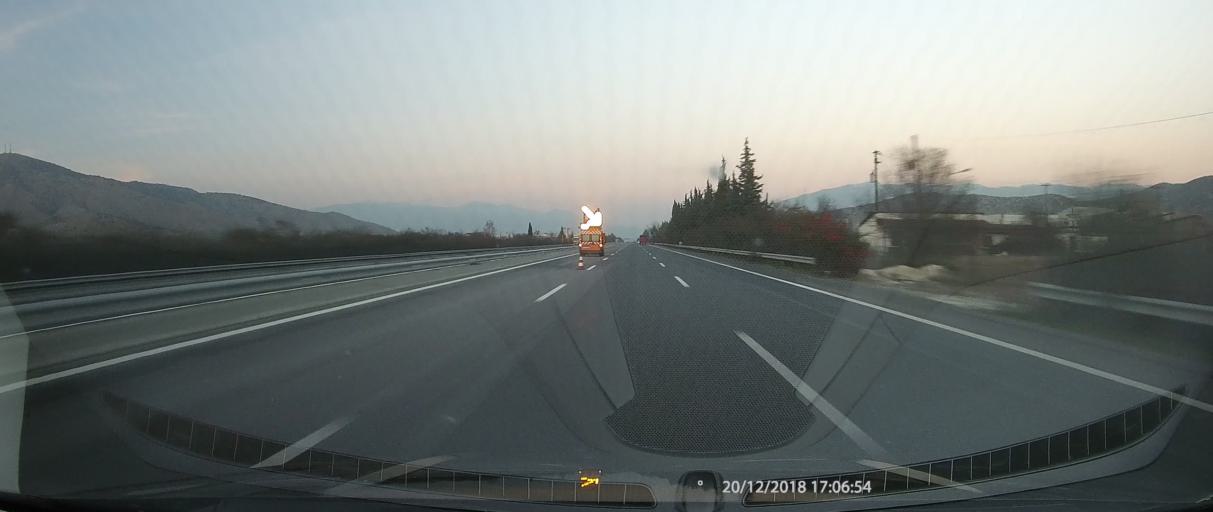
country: GR
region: Thessaly
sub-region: Nomos Larisis
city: Makrychori
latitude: 39.7672
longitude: 22.4825
